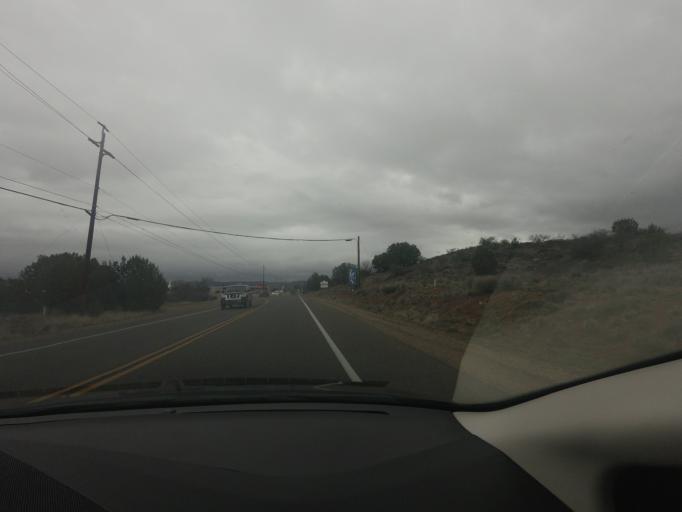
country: US
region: Arizona
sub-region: Yavapai County
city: Lake Montezuma
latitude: 34.6440
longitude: -111.7878
